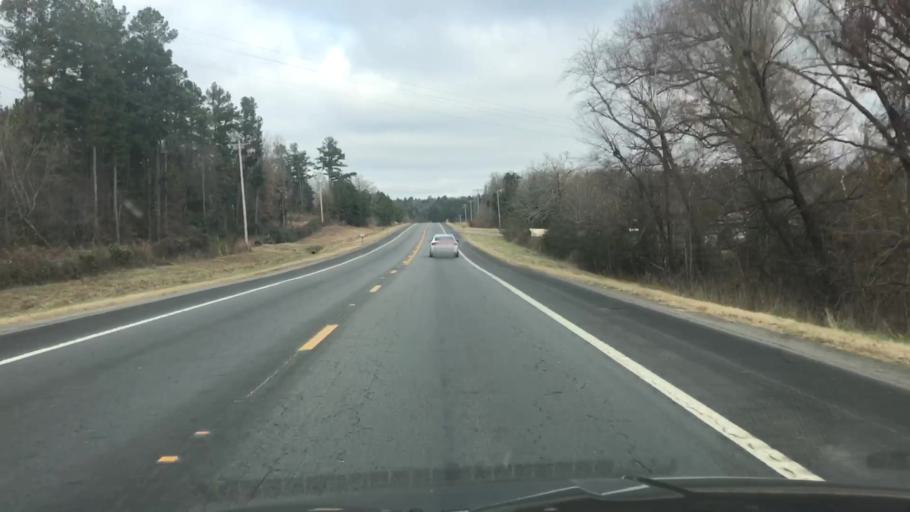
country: US
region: Arkansas
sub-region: Scott County
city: Waldron
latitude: 34.8317
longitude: -94.0421
